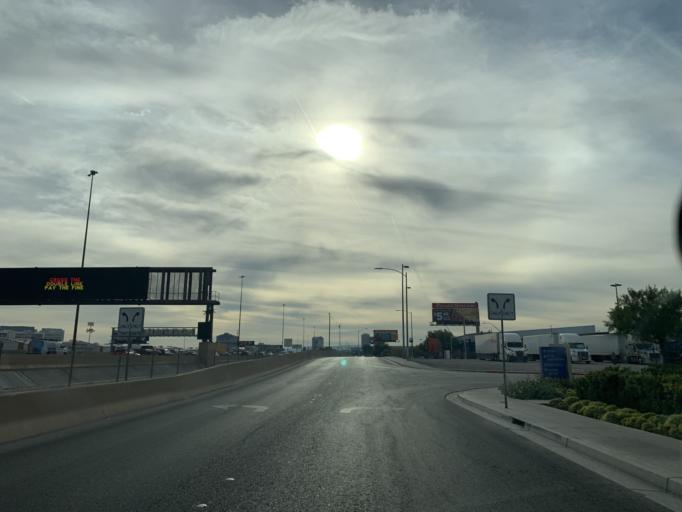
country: US
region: Nevada
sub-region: Clark County
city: Las Vegas
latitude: 36.1410
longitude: -115.1746
